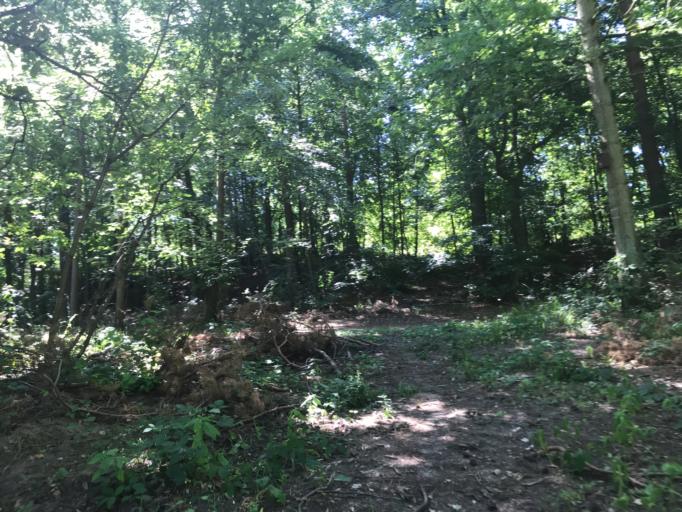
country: DE
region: Rheinland-Pfalz
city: Budenheim
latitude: 50.0150
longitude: 8.1630
